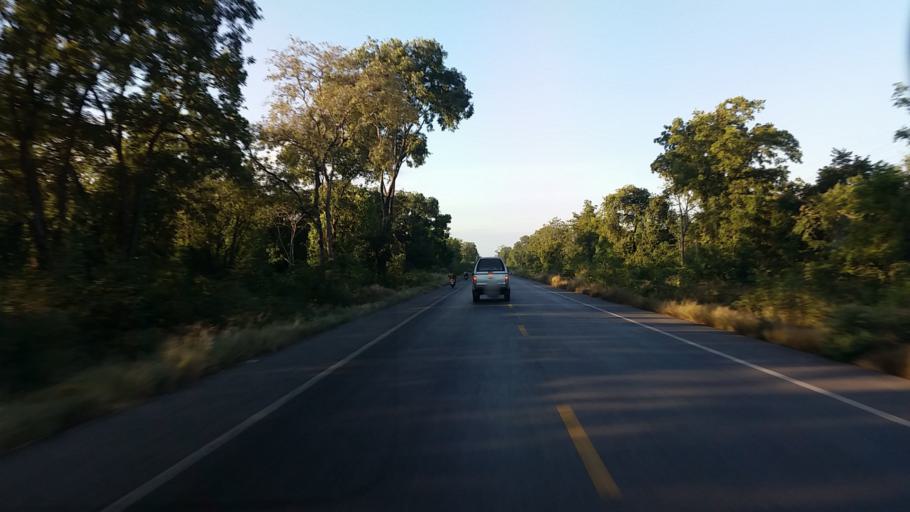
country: TH
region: Lop Buri
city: Chai Badan
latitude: 15.2430
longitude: 101.1668
